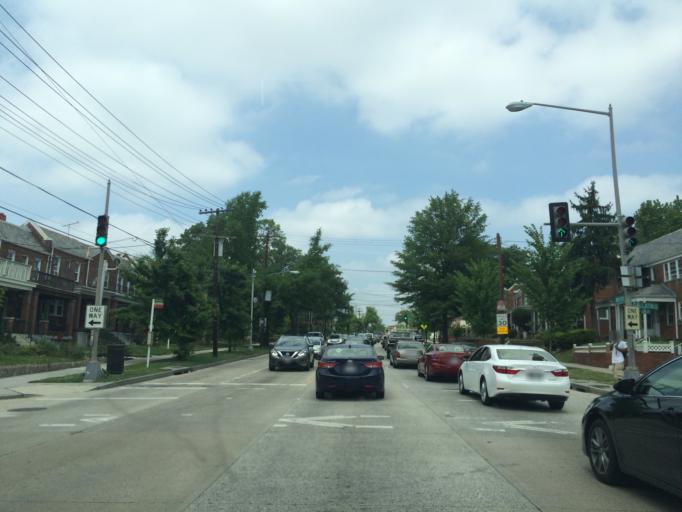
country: US
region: Maryland
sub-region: Prince George's County
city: Chillum
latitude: 38.9524
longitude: -77.0090
